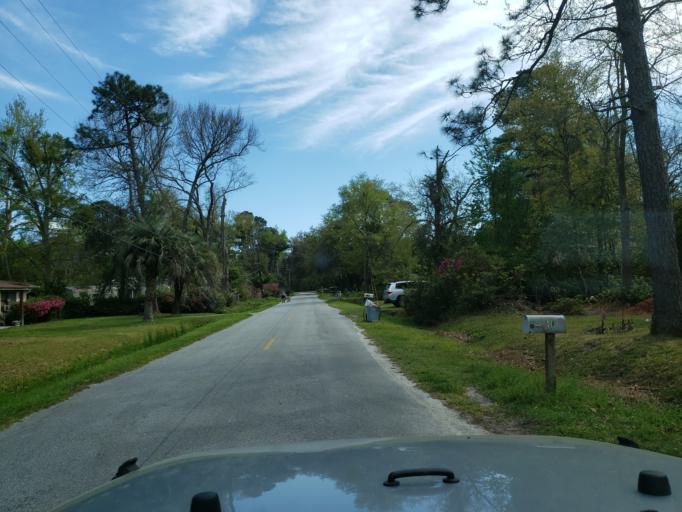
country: US
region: Georgia
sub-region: Chatham County
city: Montgomery
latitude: 31.9492
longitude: -81.1134
